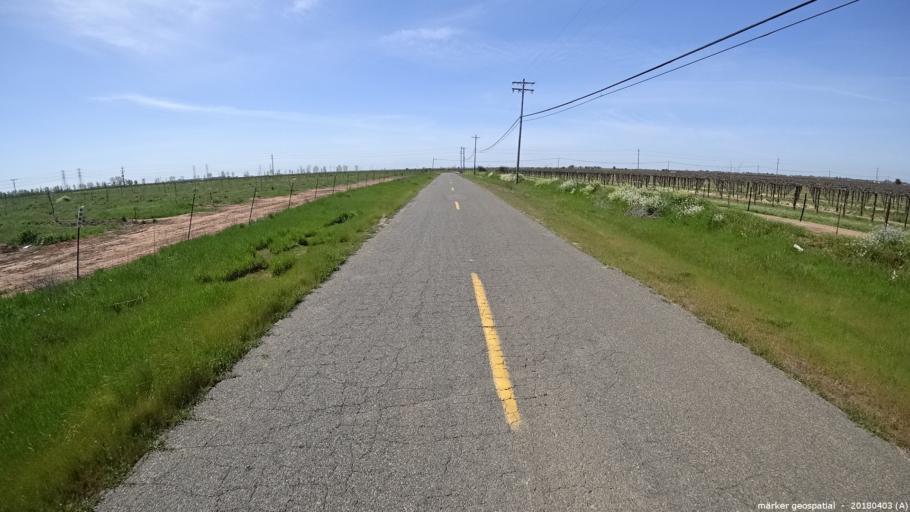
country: US
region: California
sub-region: Sacramento County
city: Herald
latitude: 38.3579
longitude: -121.2400
